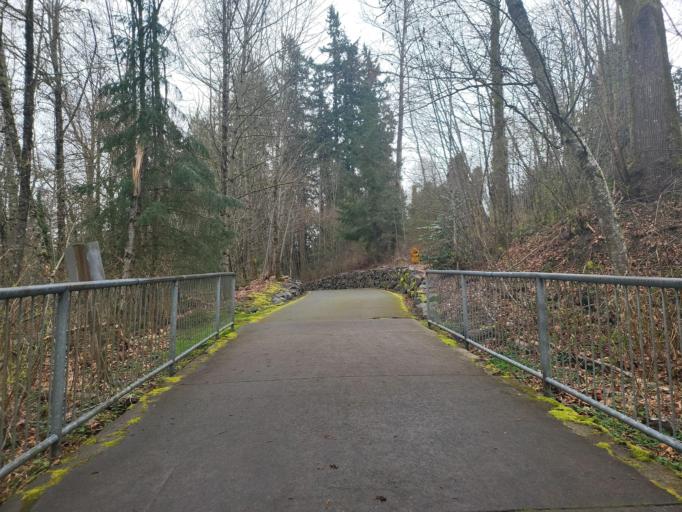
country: US
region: Washington
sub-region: King County
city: East Hill-Meridian
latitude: 47.4219
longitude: -122.1678
